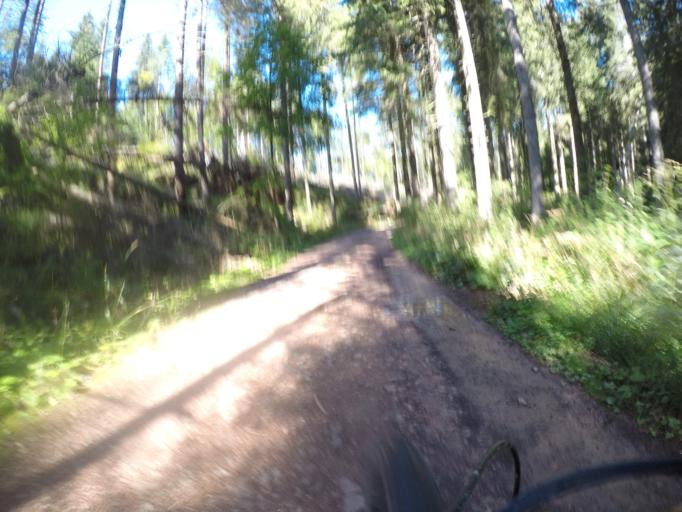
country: IT
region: Veneto
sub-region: Provincia di Vicenza
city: Canove di Roana
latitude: 45.8346
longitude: 11.5024
